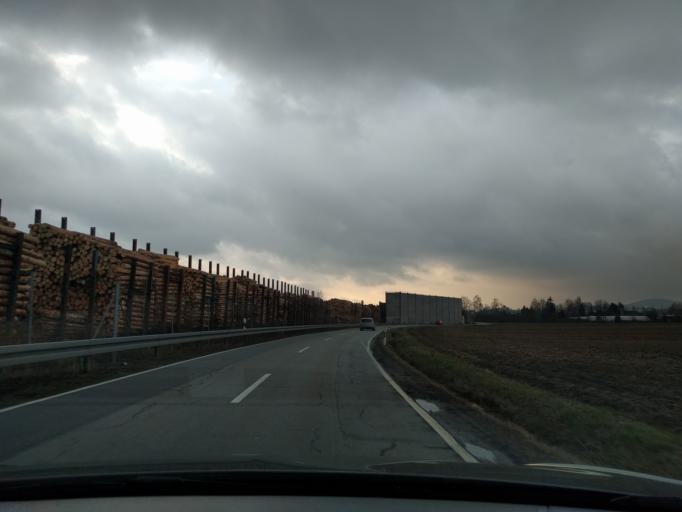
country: DE
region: Bavaria
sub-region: Lower Bavaria
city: Hengersberg
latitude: 48.7653
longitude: 13.0697
